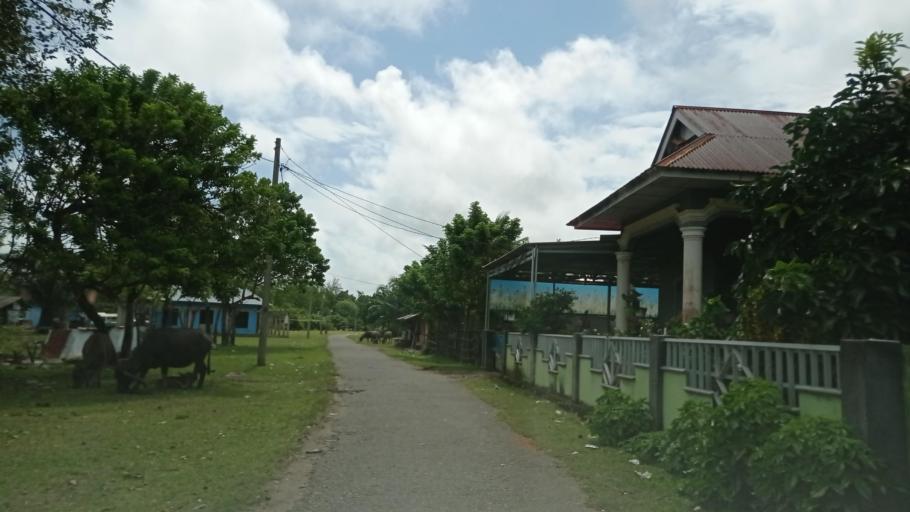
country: ID
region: Jambi
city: Sungai Penuh
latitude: -2.5481
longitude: 101.0864
